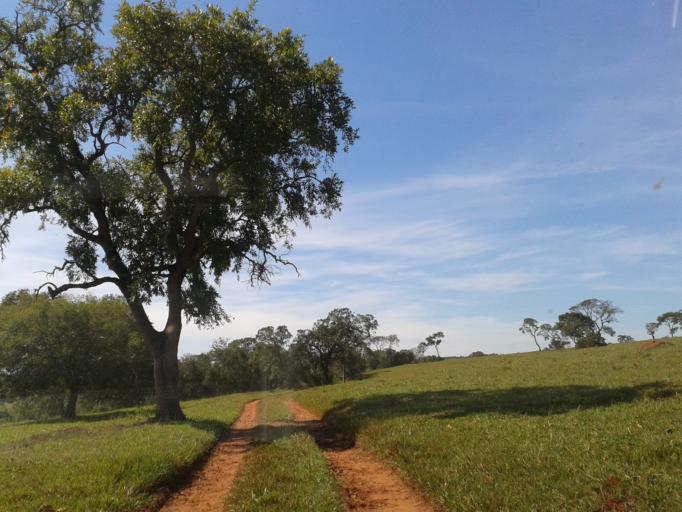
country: BR
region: Minas Gerais
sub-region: Campina Verde
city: Campina Verde
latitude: -19.4345
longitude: -49.6902
